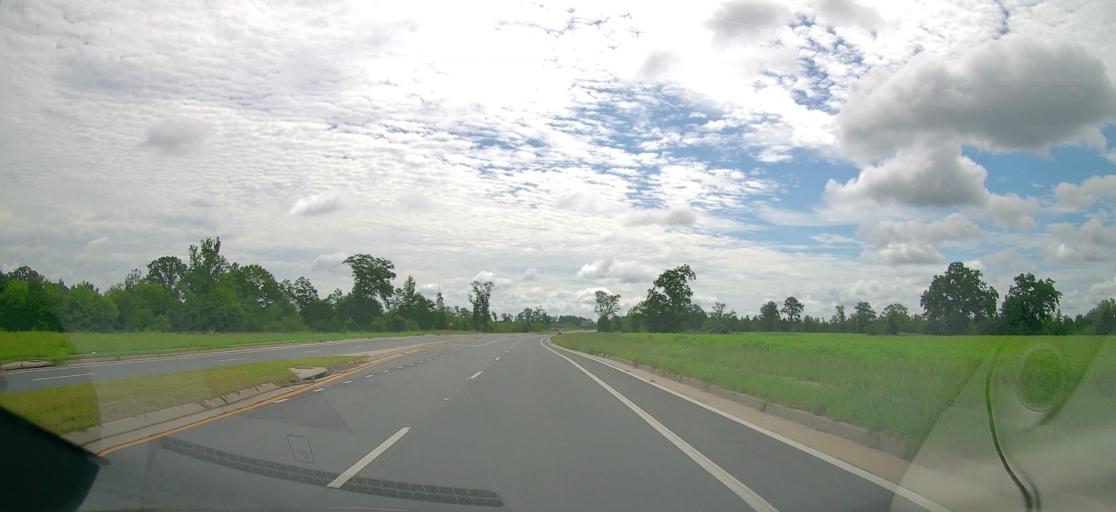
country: US
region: Georgia
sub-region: Houston County
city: Centerville
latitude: 32.6834
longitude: -83.6724
